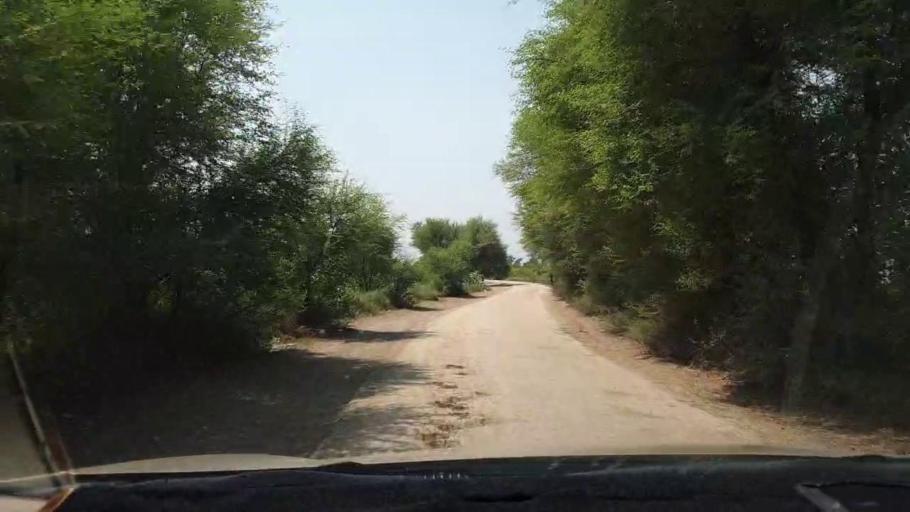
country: PK
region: Sindh
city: Larkana
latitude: 27.6273
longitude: 68.2735
